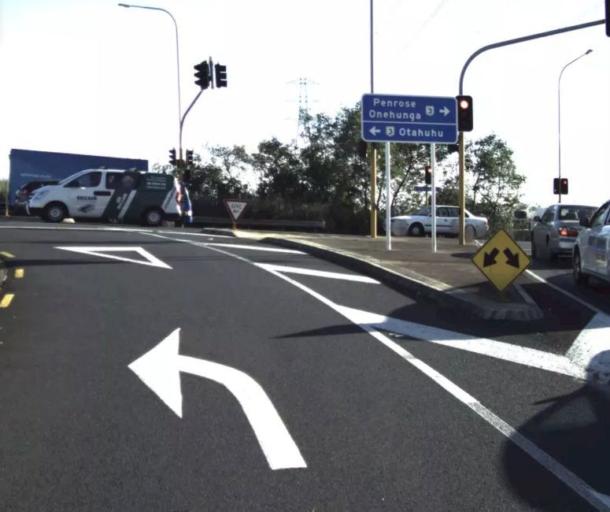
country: NZ
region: Auckland
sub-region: Auckland
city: Tamaki
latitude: -36.9252
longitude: 174.8327
